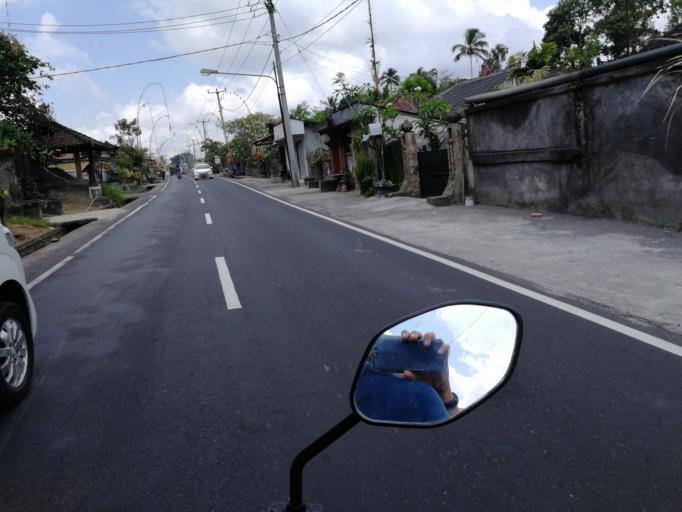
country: ID
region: Bali
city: Banjar Geriana Kangin
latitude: -8.4280
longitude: 115.4360
